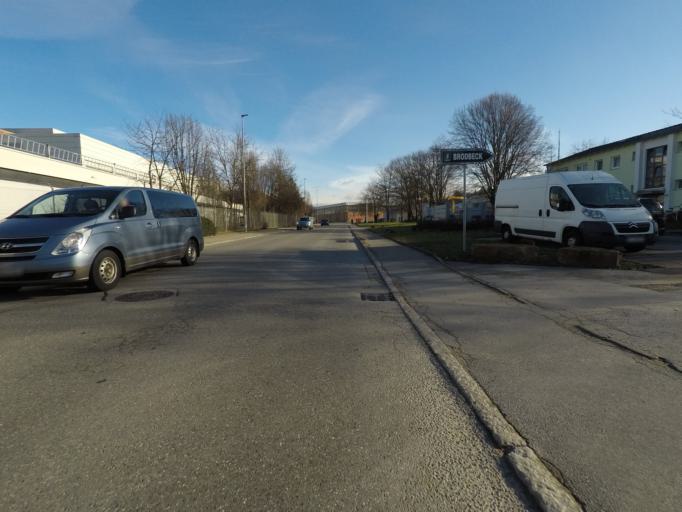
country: DE
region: Baden-Wuerttemberg
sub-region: Tuebingen Region
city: Reutlingen
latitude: 48.4940
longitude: 9.1889
